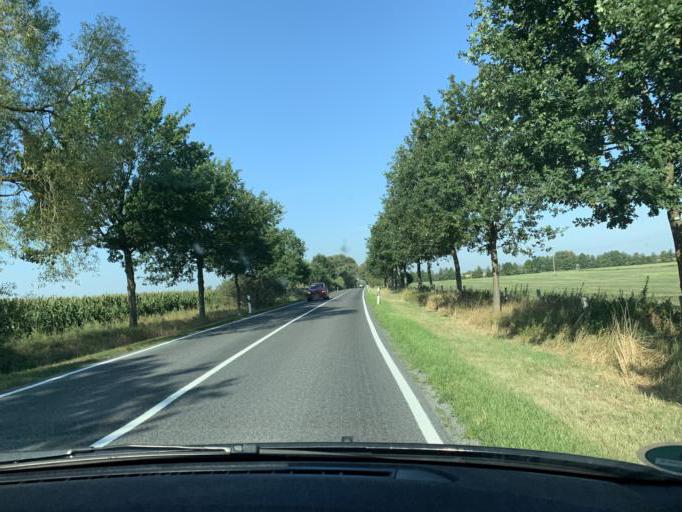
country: DE
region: Brandenburg
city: Gransee
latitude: 52.9988
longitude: 13.2192
